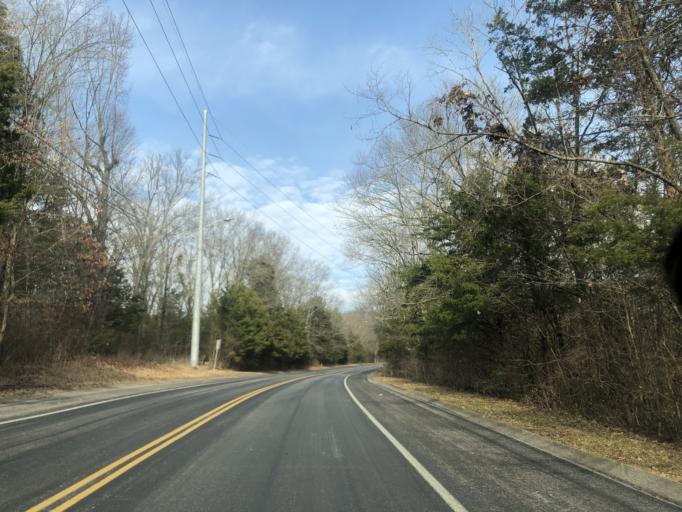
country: US
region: Tennessee
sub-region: Davidson County
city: Oak Hill
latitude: 36.1080
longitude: -86.7036
